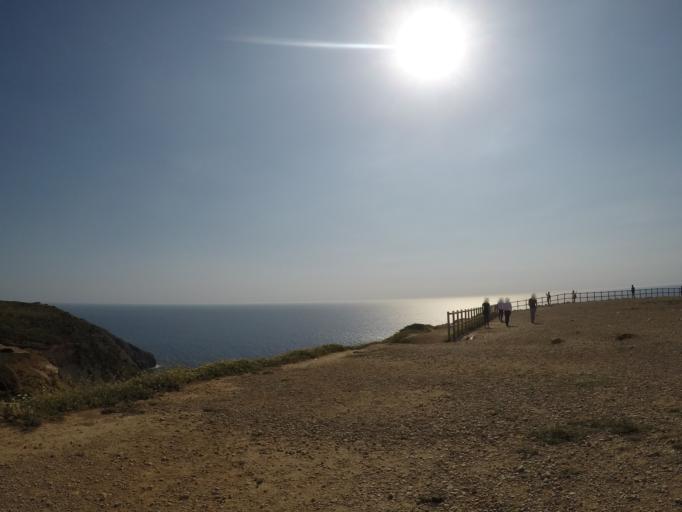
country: PT
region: Setubal
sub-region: Sesimbra
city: Sesimbra
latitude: 38.4200
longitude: -9.2162
